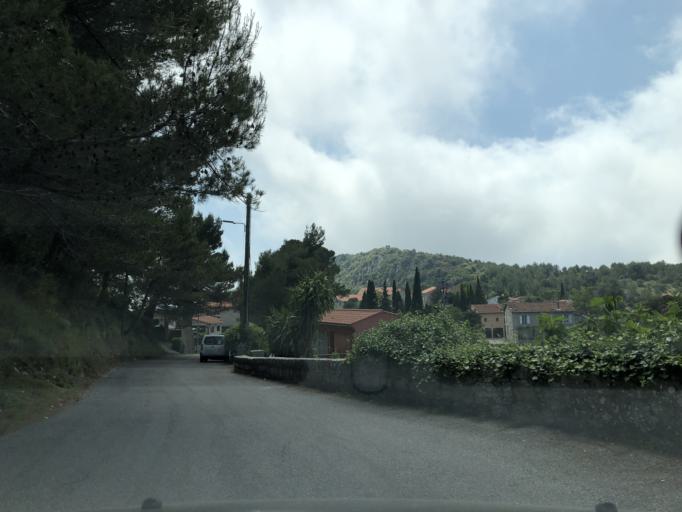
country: FR
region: Provence-Alpes-Cote d'Azur
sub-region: Departement des Alpes-Maritimes
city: Eze
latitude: 43.7350
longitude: 7.3457
